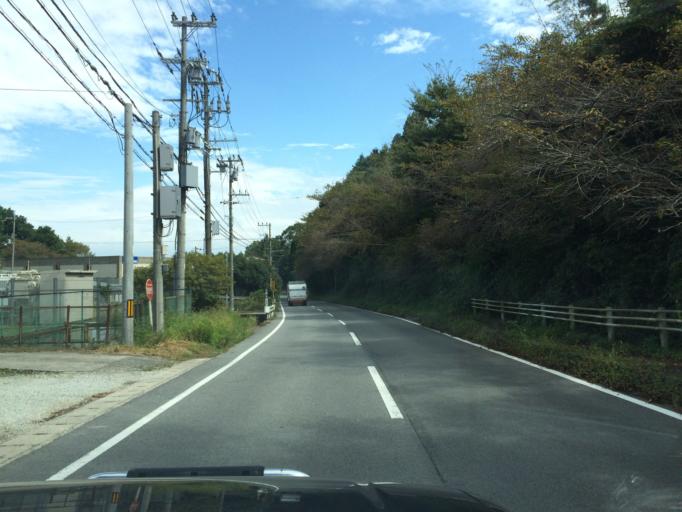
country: JP
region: Mie
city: Nabari
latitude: 34.6800
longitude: 135.9934
